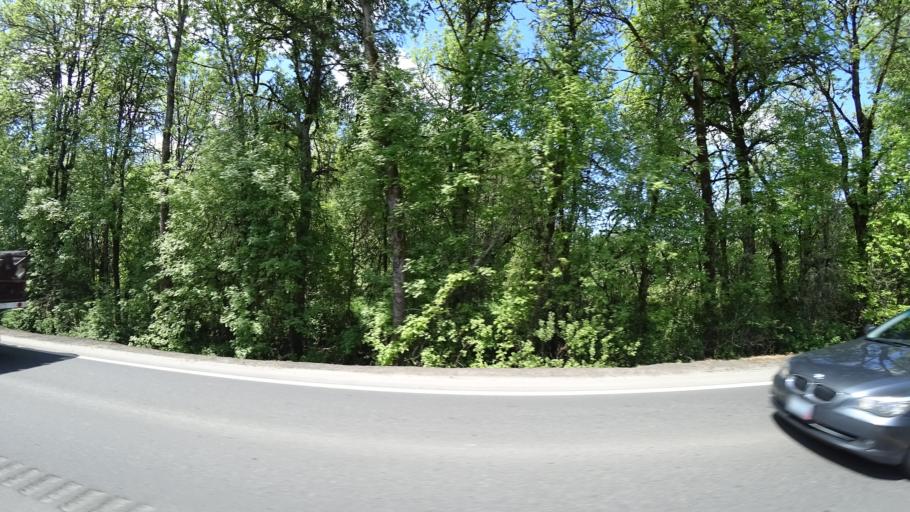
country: US
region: Oregon
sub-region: Washington County
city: Hillsboro
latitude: 45.5103
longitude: -122.9910
